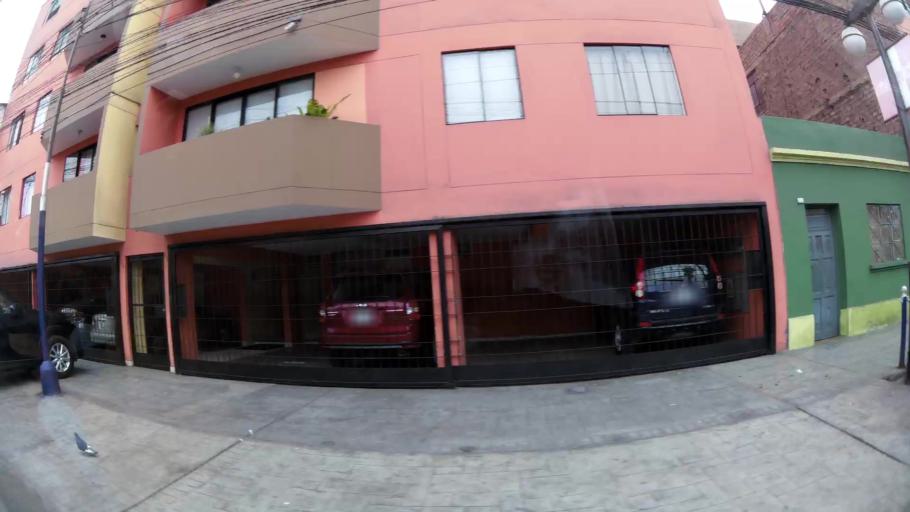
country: PE
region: Lima
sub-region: Lima
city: Surco
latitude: -12.1702
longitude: -77.0283
